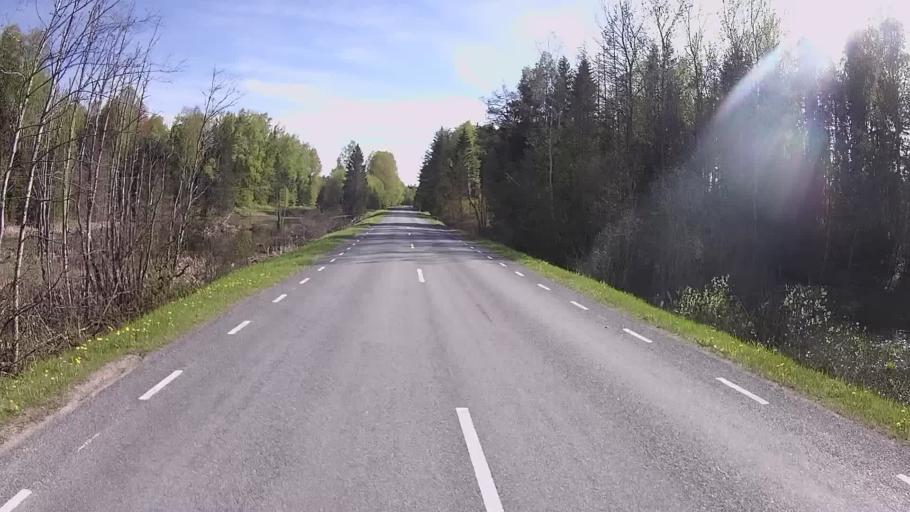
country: EE
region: Vorumaa
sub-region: Antsla vald
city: Vana-Antsla
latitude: 57.9773
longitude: 26.4657
